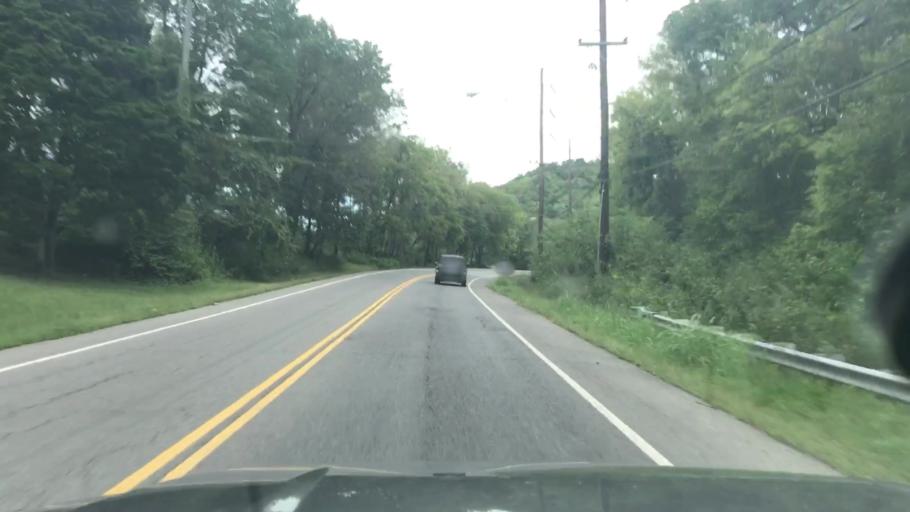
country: US
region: Tennessee
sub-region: Davidson County
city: Nashville
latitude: 36.2223
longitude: -86.8377
